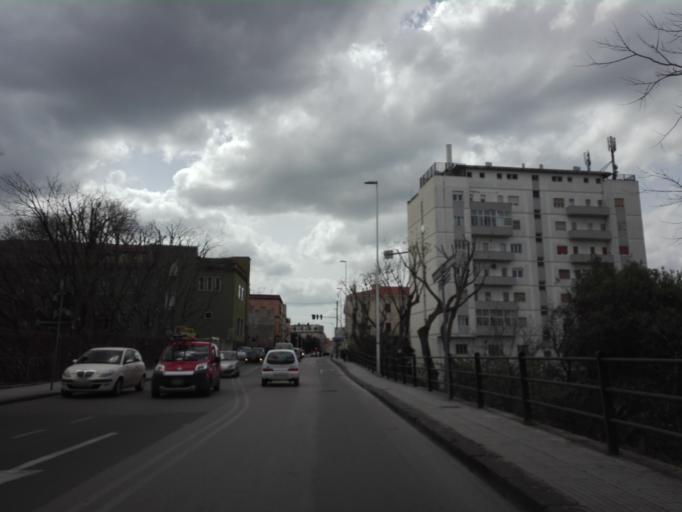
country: IT
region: Sardinia
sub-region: Provincia di Sassari
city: Sassari
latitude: 40.7320
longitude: 8.5571
